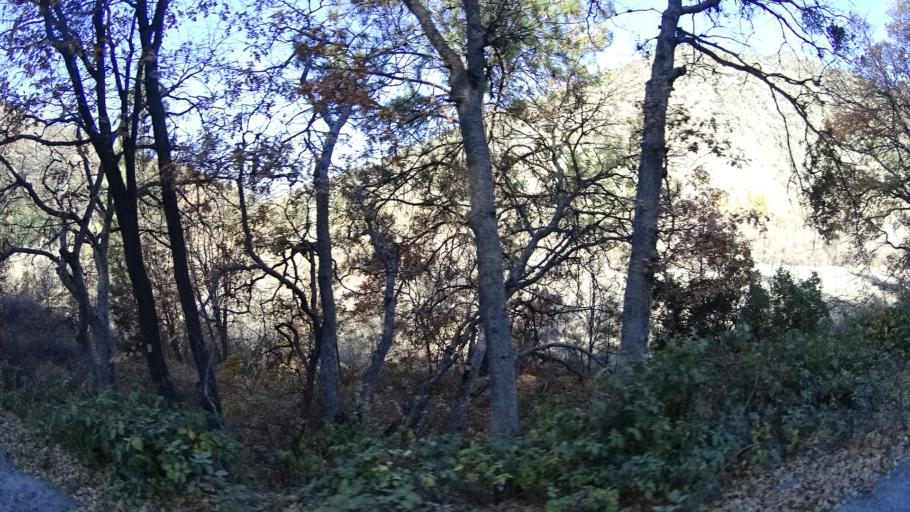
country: US
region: California
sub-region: Siskiyou County
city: Yreka
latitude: 41.8405
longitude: -122.6785
